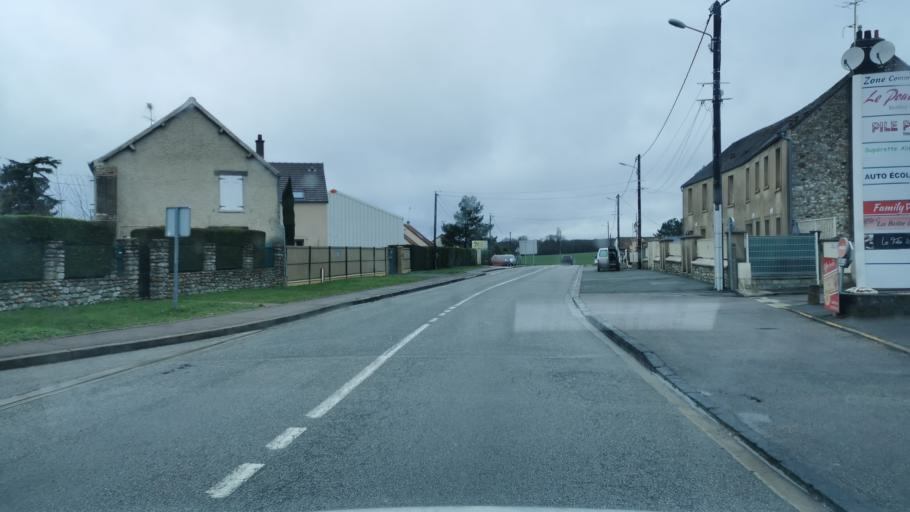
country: FR
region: Ile-de-France
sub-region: Departement des Yvelines
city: Longnes
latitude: 48.9209
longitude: 1.5839
